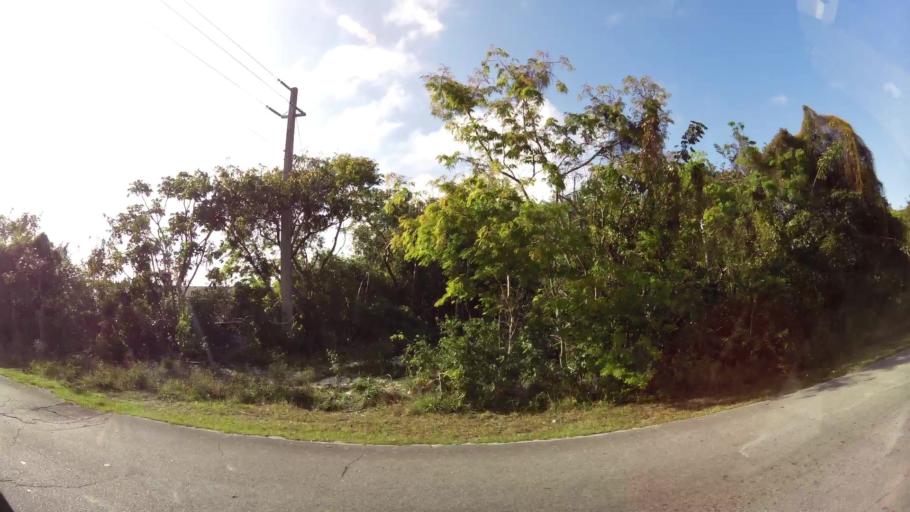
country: BS
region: Freeport
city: Lucaya
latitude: 26.5029
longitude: -78.6669
